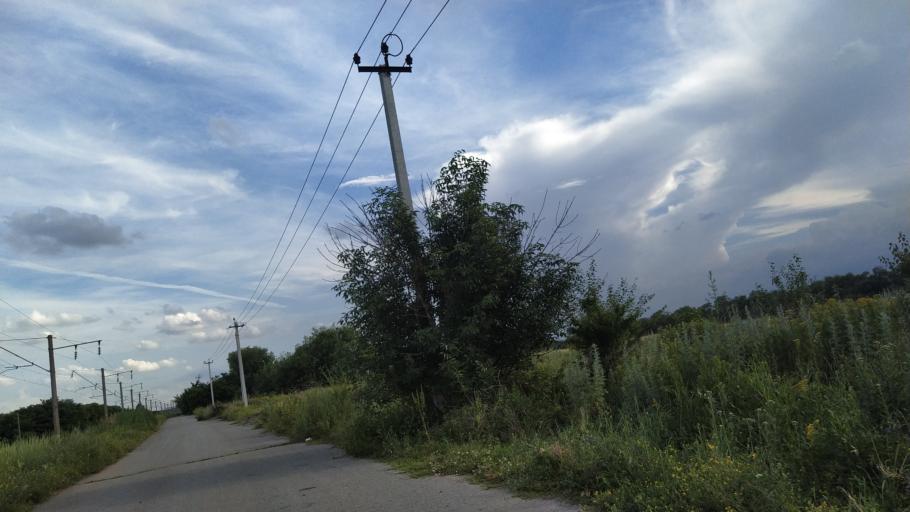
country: RU
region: Rostov
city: Bataysk
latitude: 47.1104
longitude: 39.7114
